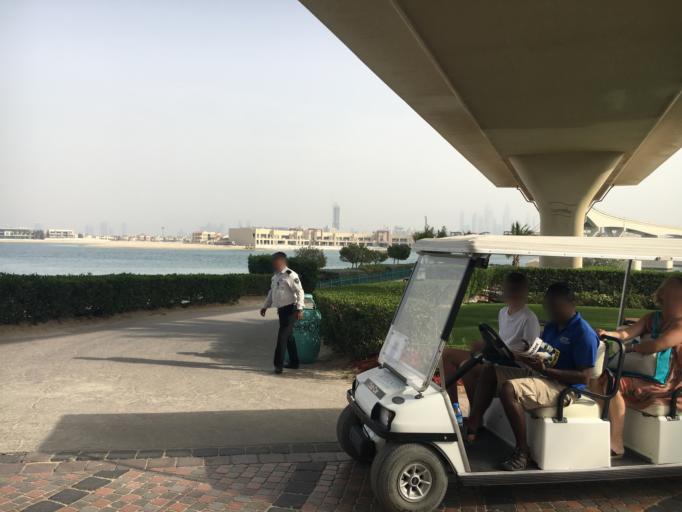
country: AE
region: Dubai
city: Dubai
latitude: 25.1317
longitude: 55.1195
